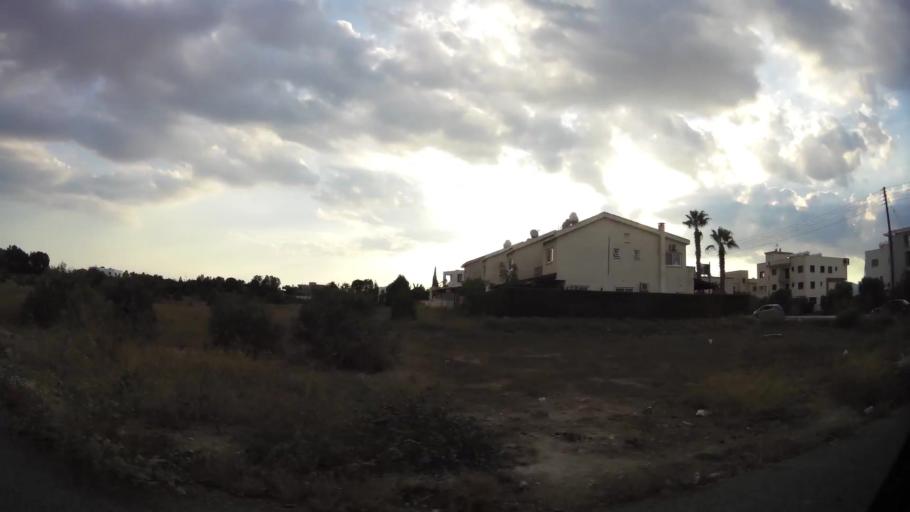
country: CY
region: Larnaka
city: Meneou
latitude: 34.8549
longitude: 33.5850
